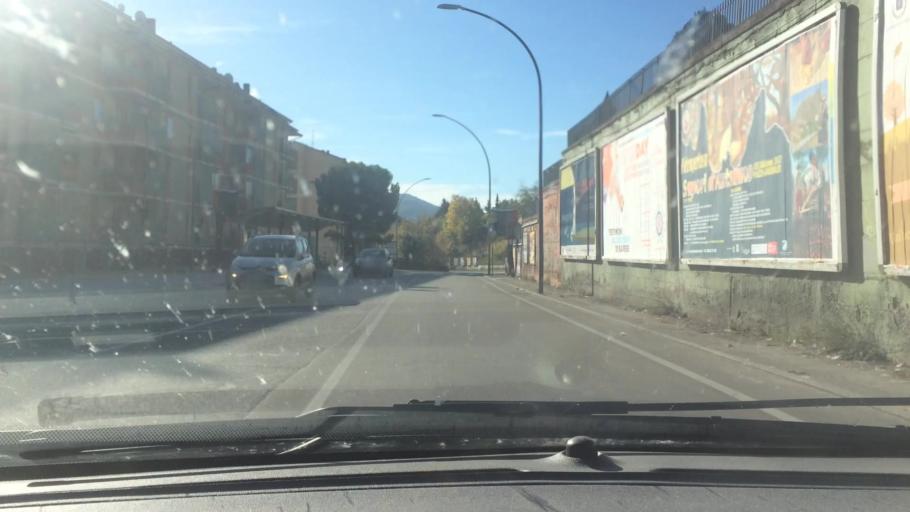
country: IT
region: Basilicate
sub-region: Provincia di Potenza
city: Potenza
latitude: 40.6451
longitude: 15.7954
